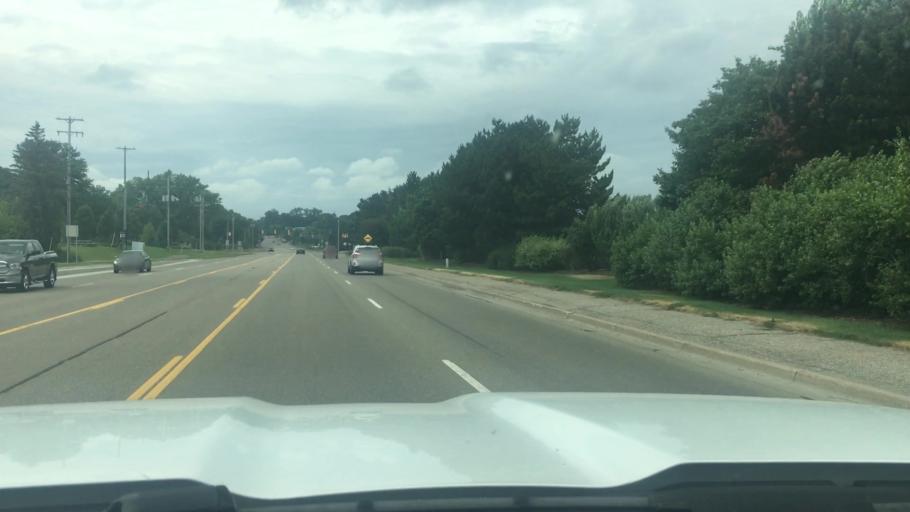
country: US
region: Michigan
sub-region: Kent County
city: Forest Hills
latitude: 42.9587
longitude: -85.4930
